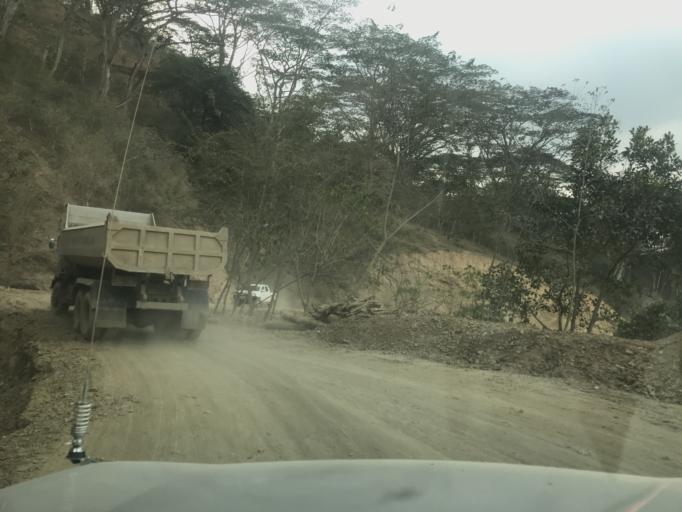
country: TL
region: Ermera
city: Gleno
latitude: -8.7636
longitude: 125.4335
